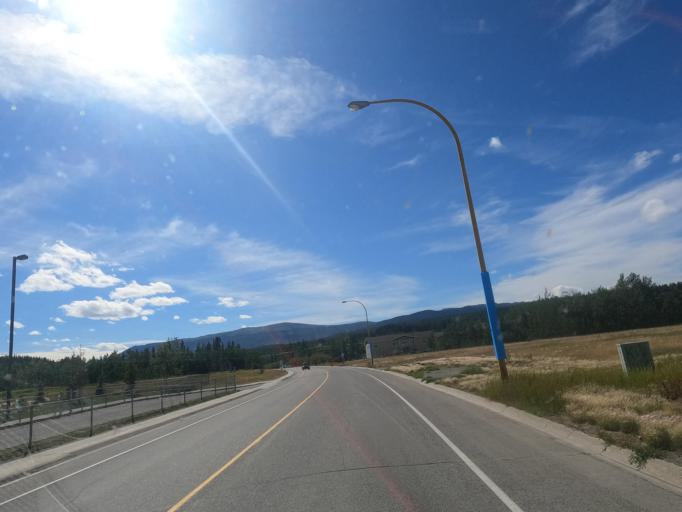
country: CA
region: Yukon
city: Whitehorse
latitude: 60.7051
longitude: -135.0366
